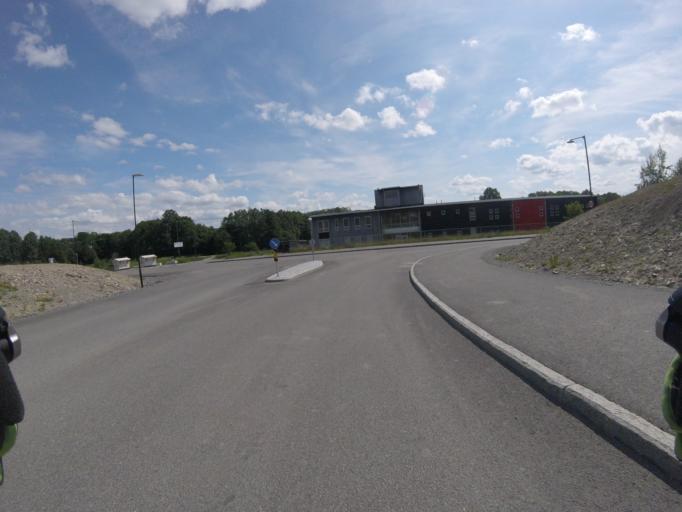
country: NO
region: Akershus
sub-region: Skedsmo
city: Lillestrom
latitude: 59.9780
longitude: 11.0401
